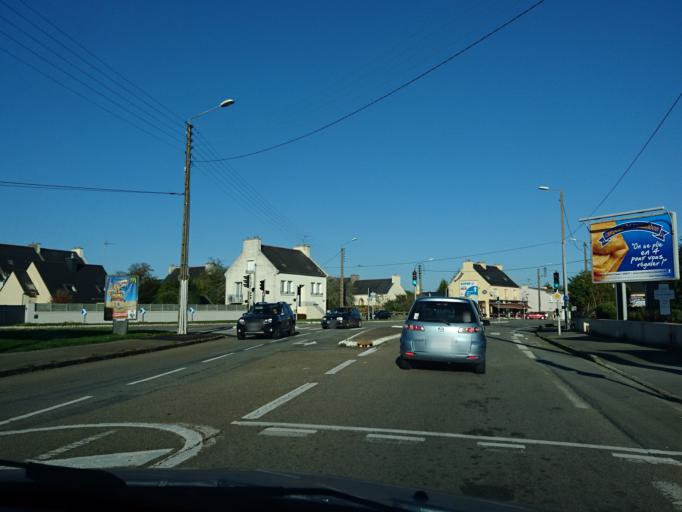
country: FR
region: Brittany
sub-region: Departement du Finistere
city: Brest
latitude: 48.4126
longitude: -4.4518
